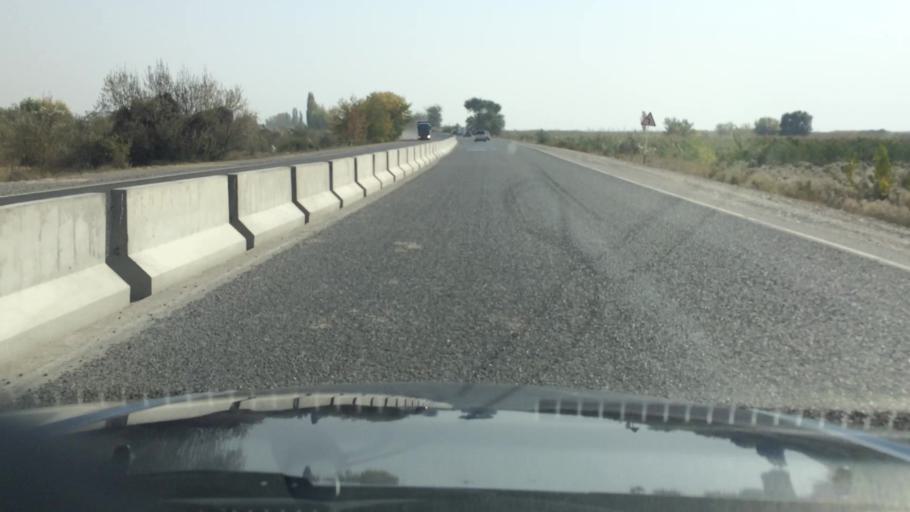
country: KG
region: Chuy
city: Kant
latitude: 42.9599
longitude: 74.9227
